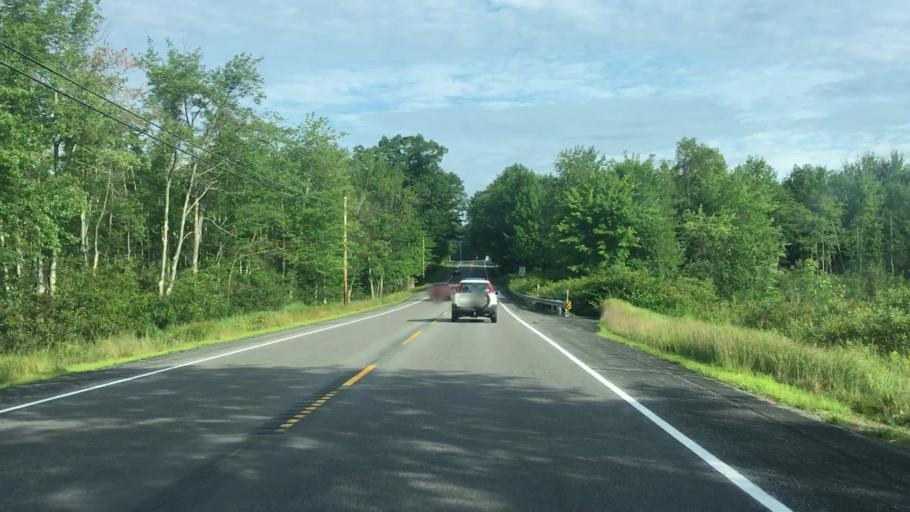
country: US
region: Maine
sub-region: York County
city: Buxton
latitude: 43.7266
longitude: -70.5348
